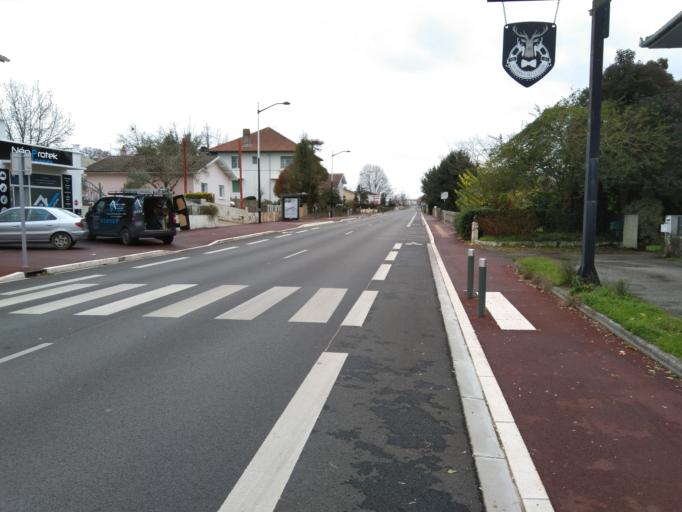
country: FR
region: Aquitaine
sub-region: Departement des Landes
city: Dax
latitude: 43.6959
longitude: -1.0680
